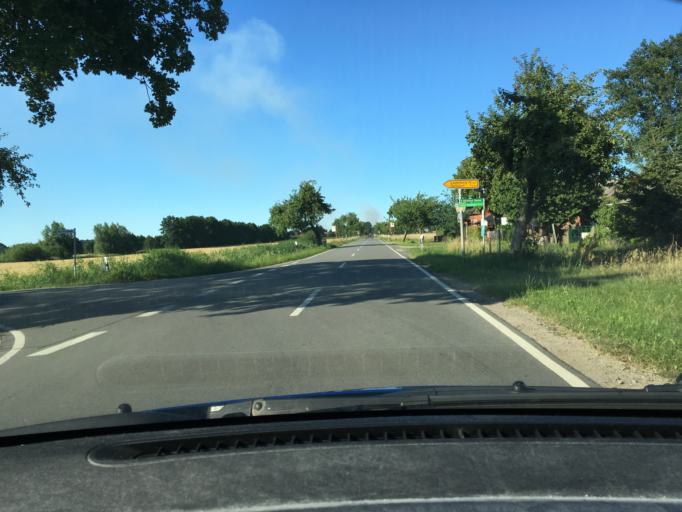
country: DE
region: Mecklenburg-Vorpommern
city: Boizenburg
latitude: 53.3474
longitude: 10.6987
